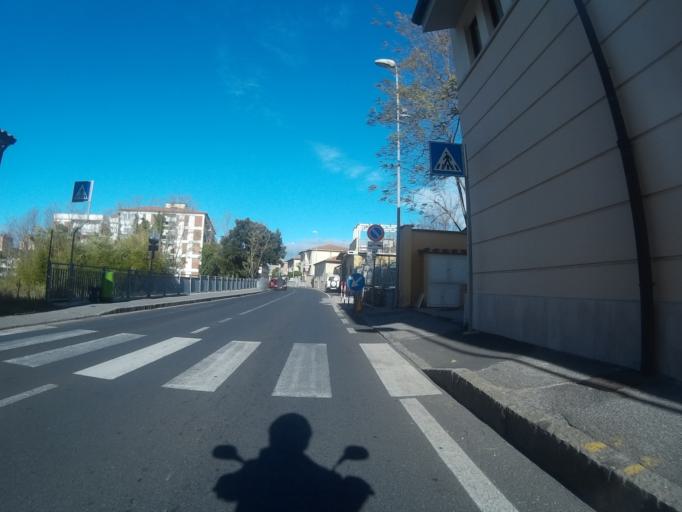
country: IT
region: Tuscany
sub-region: Provincia di Livorno
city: Livorno
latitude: 43.5342
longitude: 10.3423
